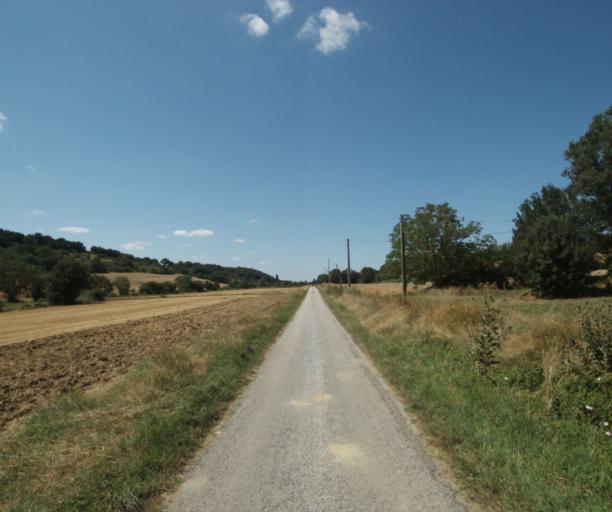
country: FR
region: Midi-Pyrenees
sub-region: Departement de la Haute-Garonne
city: Auriac-sur-Vendinelle
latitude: 43.4976
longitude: 1.8651
